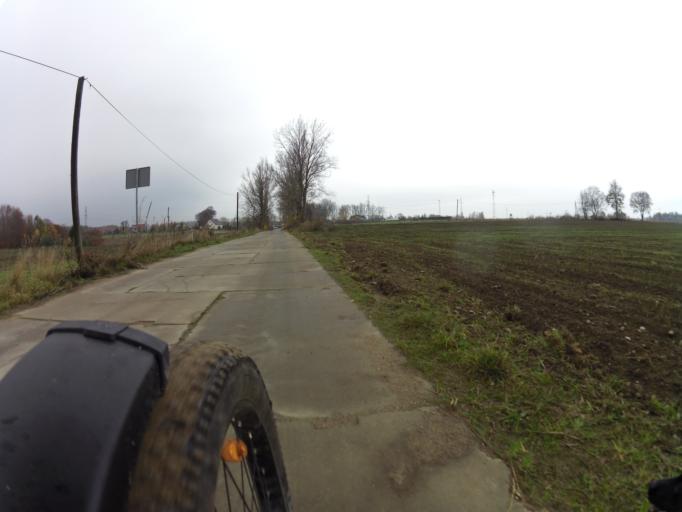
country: PL
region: Pomeranian Voivodeship
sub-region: Powiat pucki
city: Krokowa
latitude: 54.7202
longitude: 18.1383
